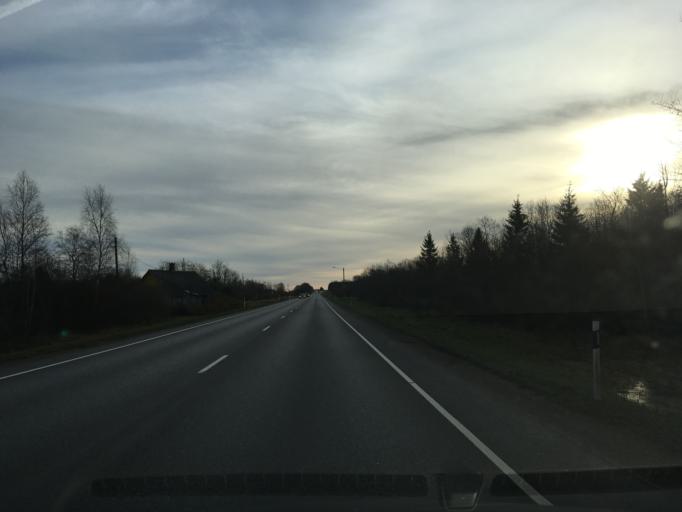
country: EE
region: Ida-Virumaa
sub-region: Kohtla-Jaerve linn
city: Kohtla-Jarve
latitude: 59.4149
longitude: 27.2970
